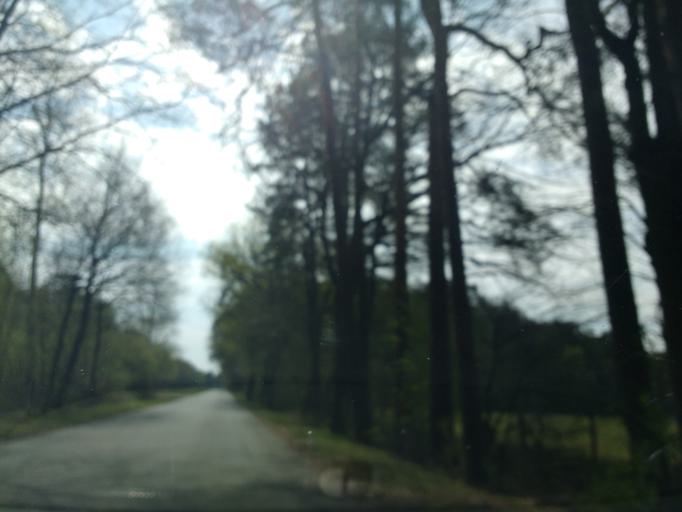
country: DE
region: North Rhine-Westphalia
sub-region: Regierungsbezirk Detmold
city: Hovelhof
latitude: 51.7916
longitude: 8.7207
